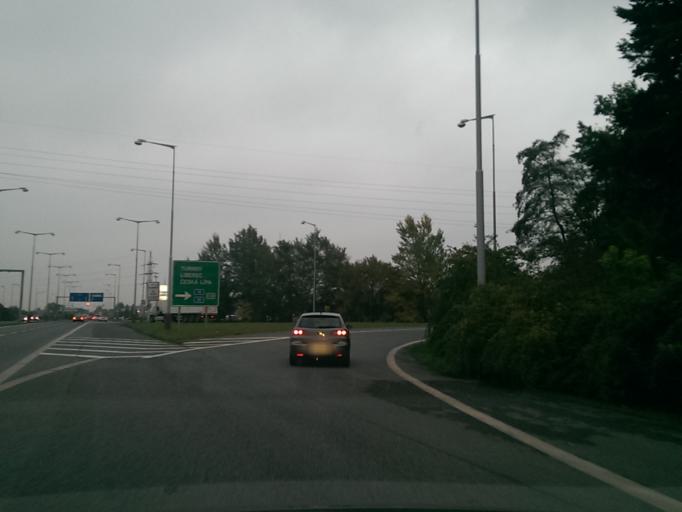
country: CZ
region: Central Bohemia
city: Kosmonosy
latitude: 50.4097
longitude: 14.9377
